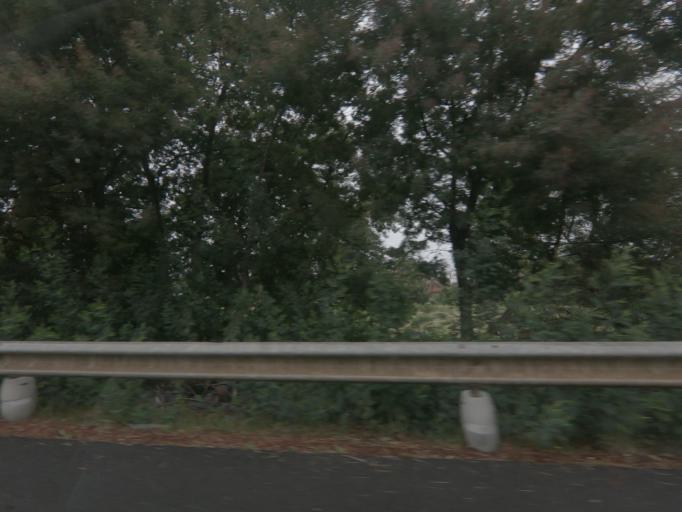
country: ES
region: Extremadura
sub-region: Provincia de Badajoz
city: Puebla de Obando
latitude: 39.1714
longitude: -6.6264
